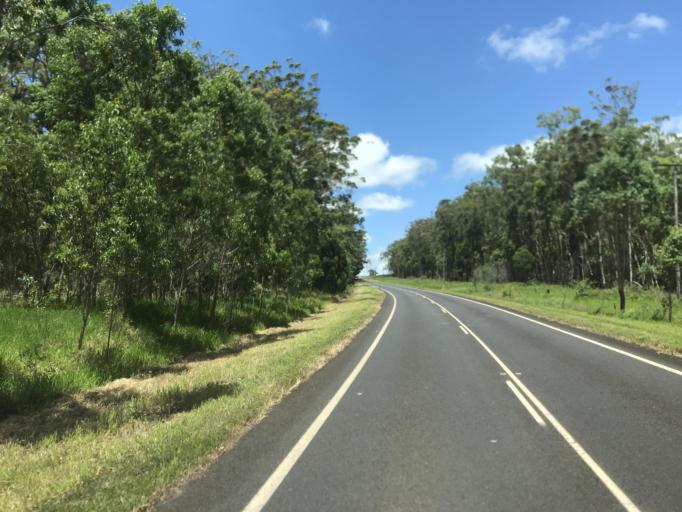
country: AU
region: Queensland
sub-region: Tablelands
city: Ravenshoe
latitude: -17.5362
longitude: 145.4518
